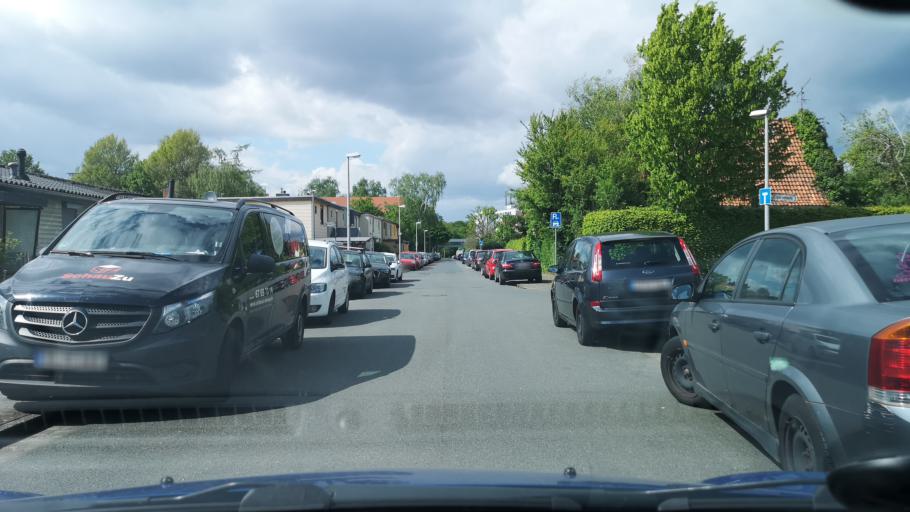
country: DE
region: Lower Saxony
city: Laatzen
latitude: 52.3336
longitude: 9.8058
